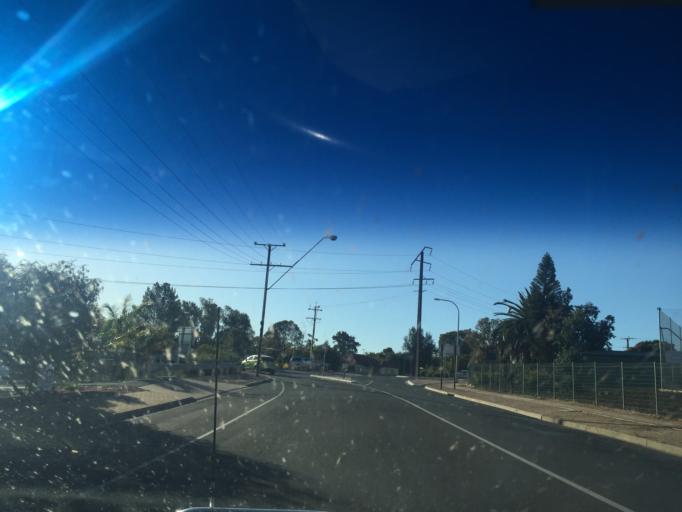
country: AU
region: South Australia
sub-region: Berri and Barmera
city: Berri
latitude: -34.2856
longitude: 140.5978
